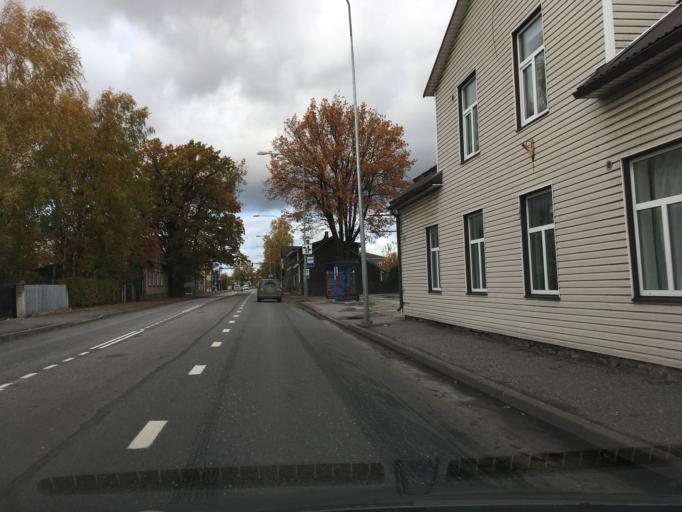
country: EE
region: Paernumaa
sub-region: Paernu linn
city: Parnu
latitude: 58.3964
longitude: 24.4942
